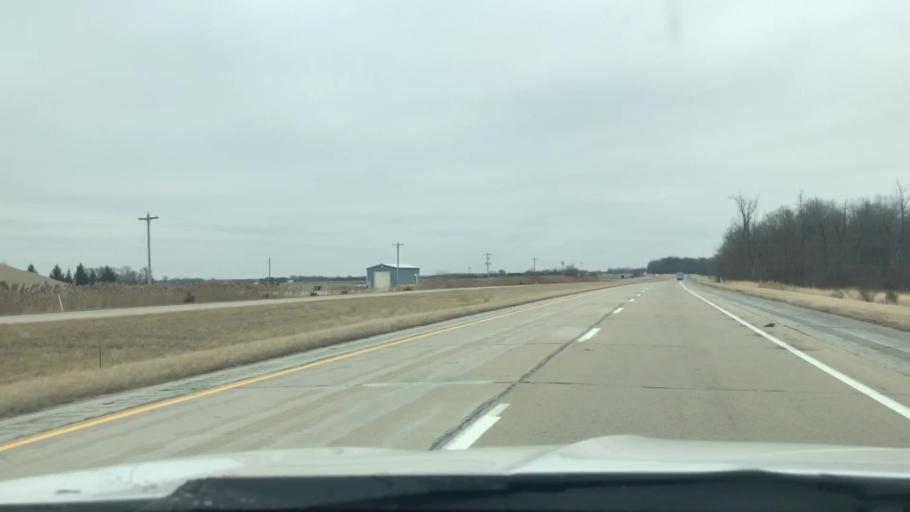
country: US
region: Indiana
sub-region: Cass County
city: Logansport
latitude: 40.7366
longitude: -86.2851
